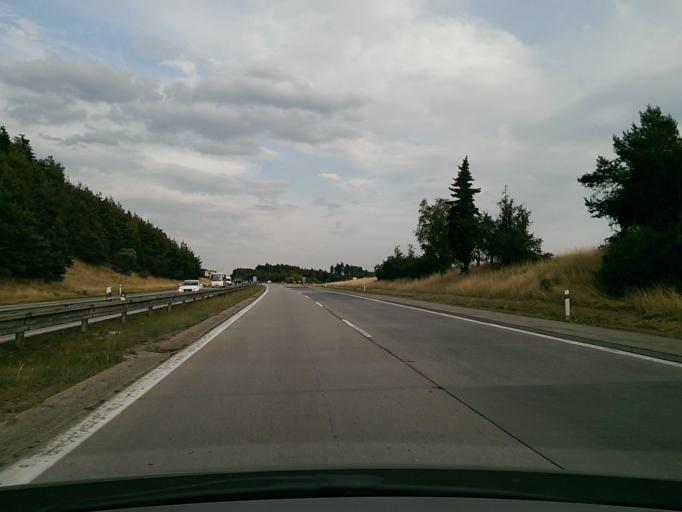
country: CZ
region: Vysocina
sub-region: Okres Zd'ar nad Sazavou
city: Velke Mezirici
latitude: 49.3382
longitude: 16.0566
